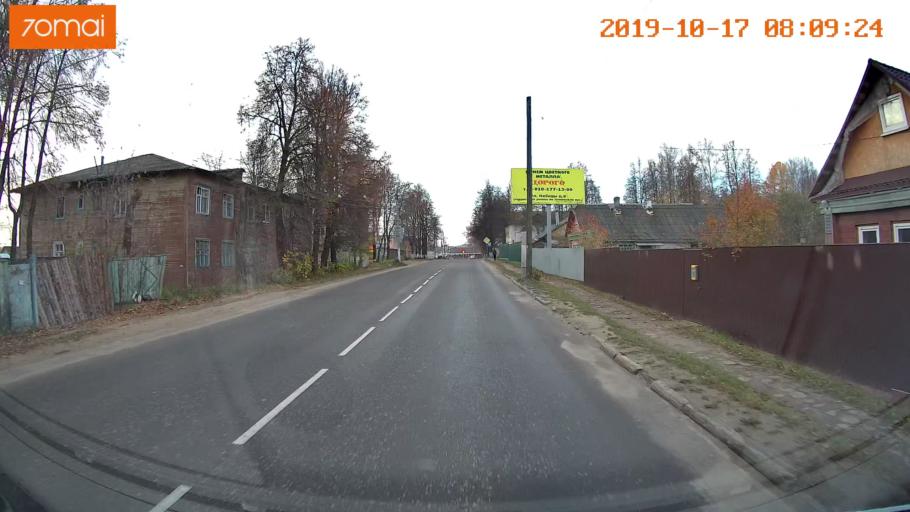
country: RU
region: Vladimir
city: Kol'chugino
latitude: 56.3122
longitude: 39.3806
